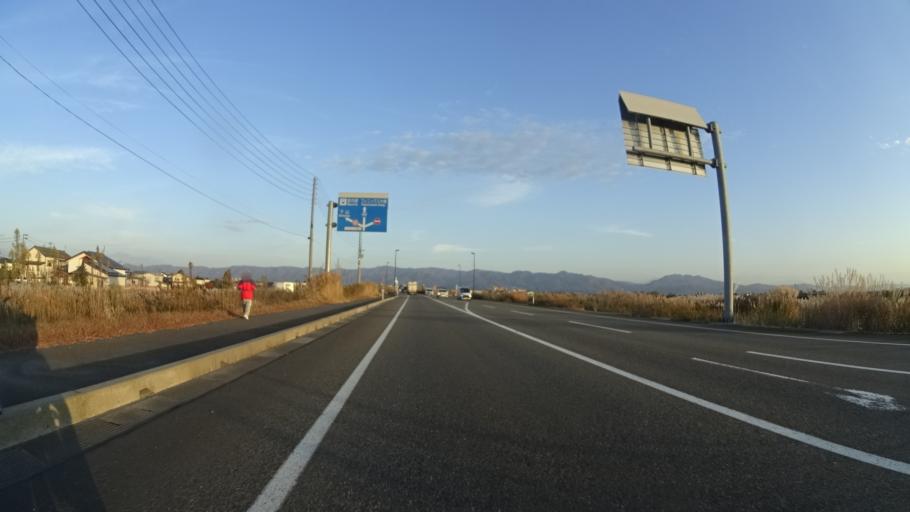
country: JP
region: Niigata
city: Nagaoka
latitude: 37.4350
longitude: 138.8066
